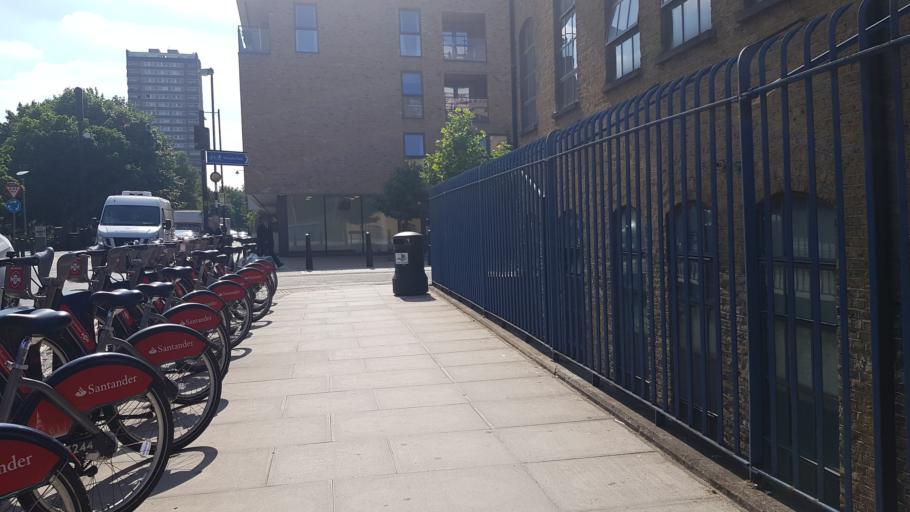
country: GB
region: England
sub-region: Greater London
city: Hackney
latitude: 51.5351
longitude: -0.0335
